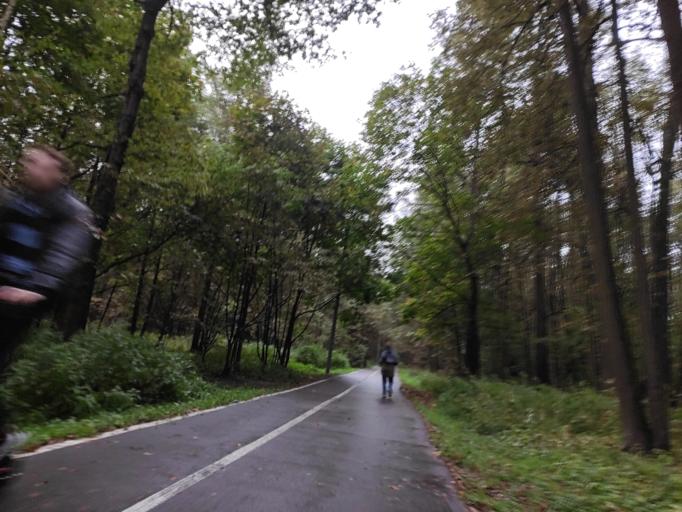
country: RU
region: Moskovskaya
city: Izmaylovo
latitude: 55.7719
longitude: 37.7831
